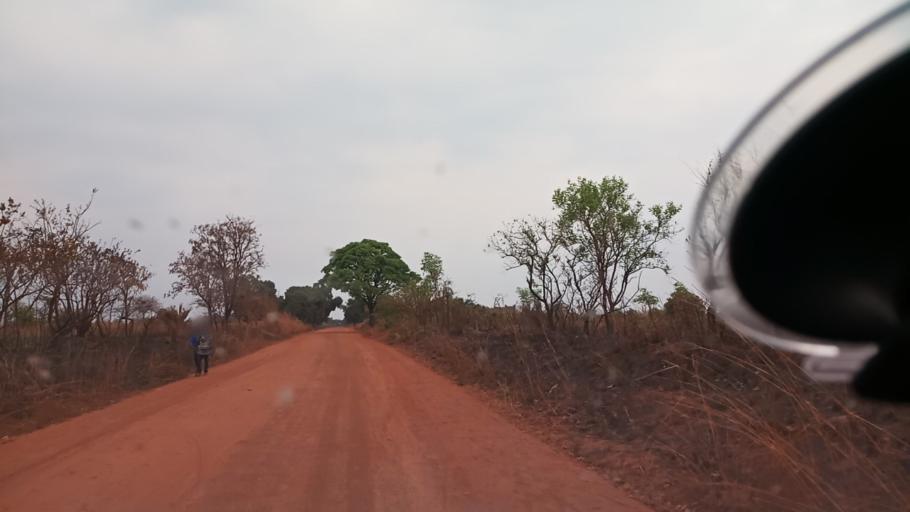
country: ZM
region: Luapula
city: Nchelenge
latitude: -9.1679
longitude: 28.2815
